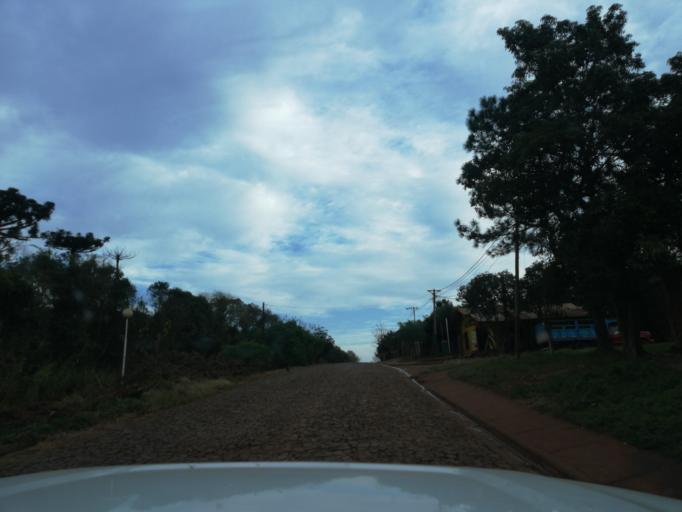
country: AR
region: Misiones
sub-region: Departamento de San Pedro
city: San Pedro
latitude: -26.6265
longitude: -54.0953
